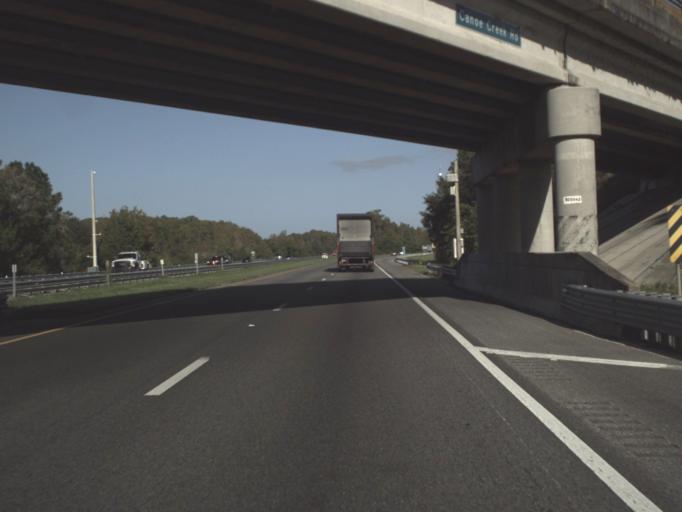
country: US
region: Florida
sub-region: Osceola County
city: Saint Cloud
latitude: 28.0864
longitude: -81.2655
